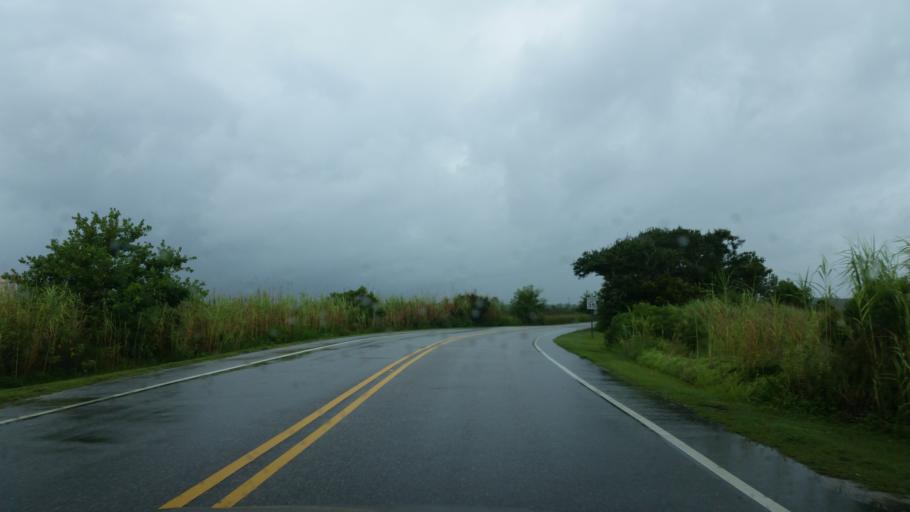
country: US
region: Alabama
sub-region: Baldwin County
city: Gulf Shores
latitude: 30.2544
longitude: -87.6685
